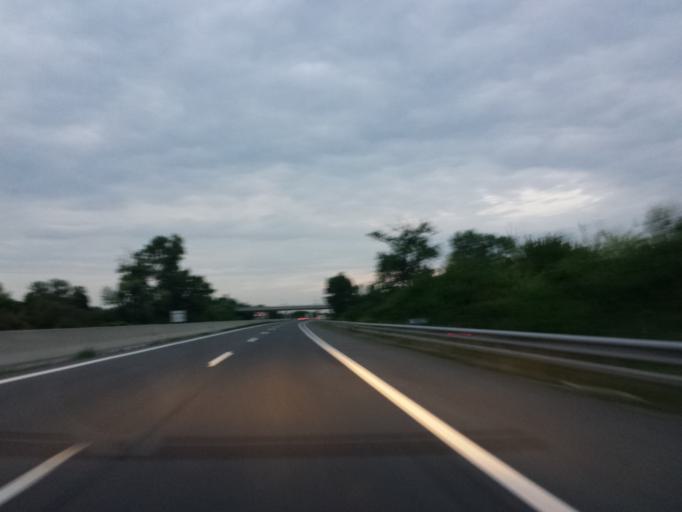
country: AT
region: Lower Austria
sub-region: Politischer Bezirk Baden
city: Trumau
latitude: 47.9691
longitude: 16.3678
